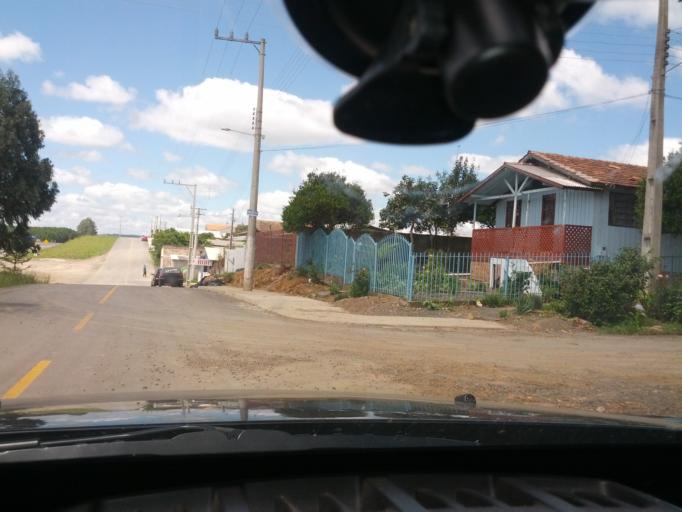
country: BR
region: Santa Catarina
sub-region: Lages
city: Lages
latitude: -27.7929
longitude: -50.2793
